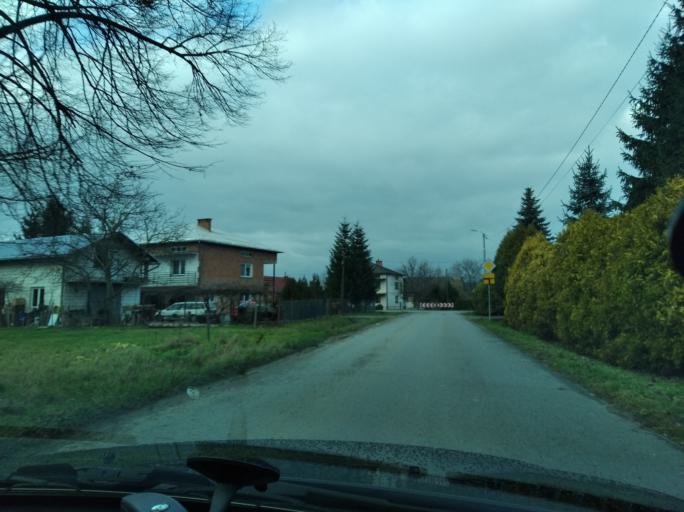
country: PL
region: Subcarpathian Voivodeship
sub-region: Powiat lancucki
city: Gluchow
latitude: 50.1069
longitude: 22.2834
